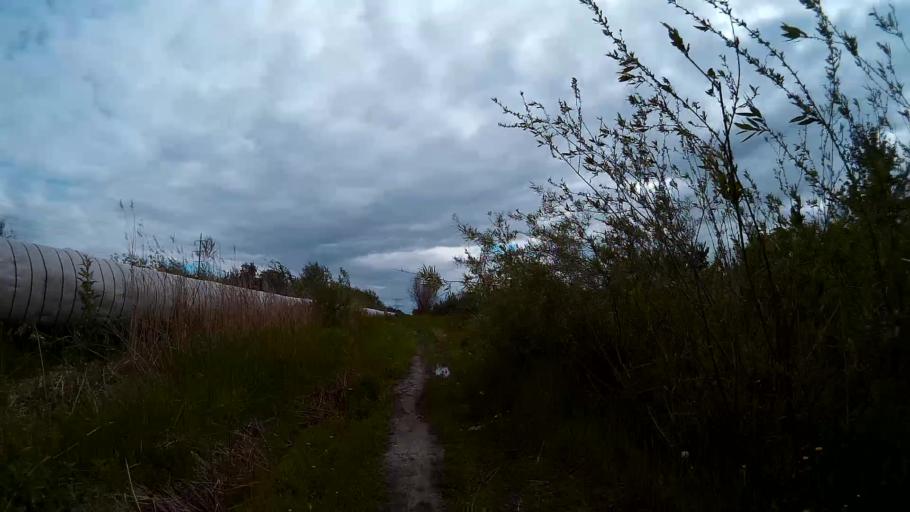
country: RU
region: Ulyanovsk
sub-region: Ulyanovskiy Rayon
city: Ulyanovsk
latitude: 54.2454
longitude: 48.3005
